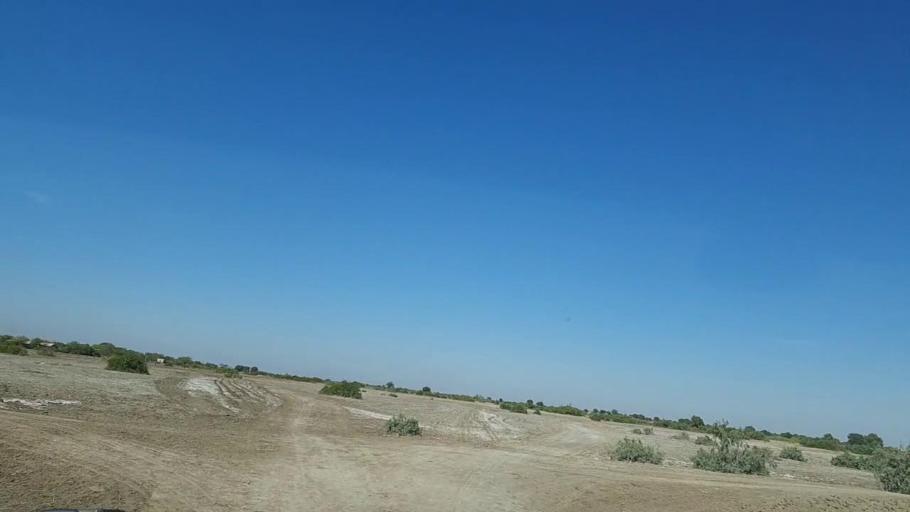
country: PK
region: Sindh
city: Pithoro
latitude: 25.5544
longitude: 69.4600
